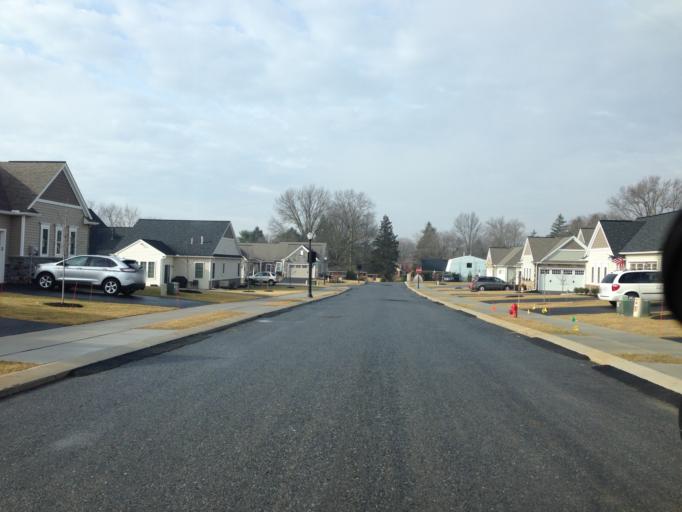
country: US
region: Pennsylvania
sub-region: Lancaster County
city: Lititz
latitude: 40.1492
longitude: -76.2936
